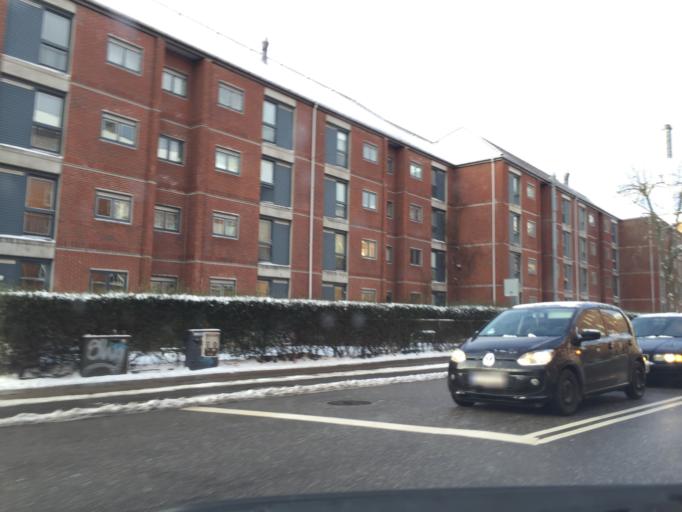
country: DK
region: Capital Region
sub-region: Kobenhavn
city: Christianshavn
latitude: 55.6583
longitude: 12.6029
